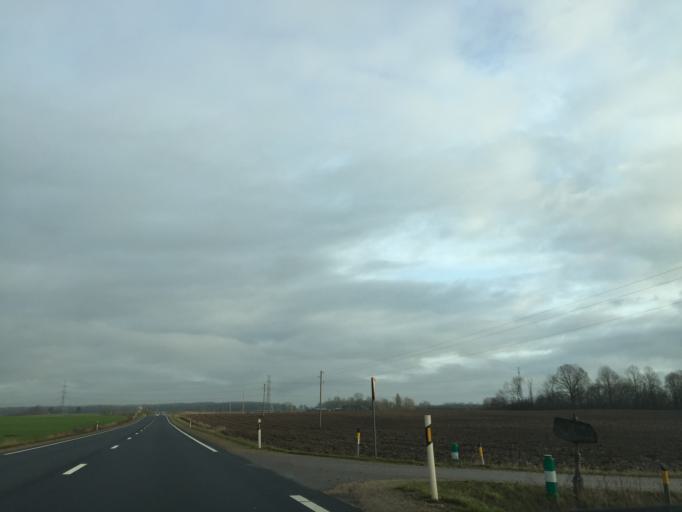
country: LV
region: Durbe
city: Liegi
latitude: 56.5678
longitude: 21.2757
